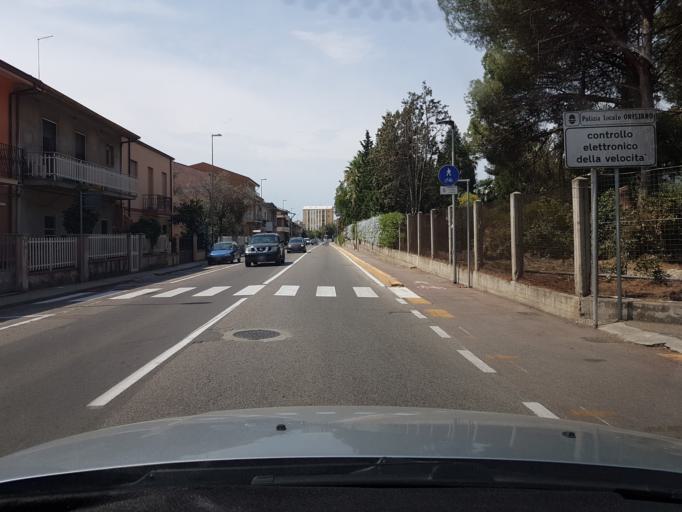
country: IT
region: Sardinia
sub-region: Provincia di Oristano
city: Oristano
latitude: 39.9094
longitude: 8.6031
